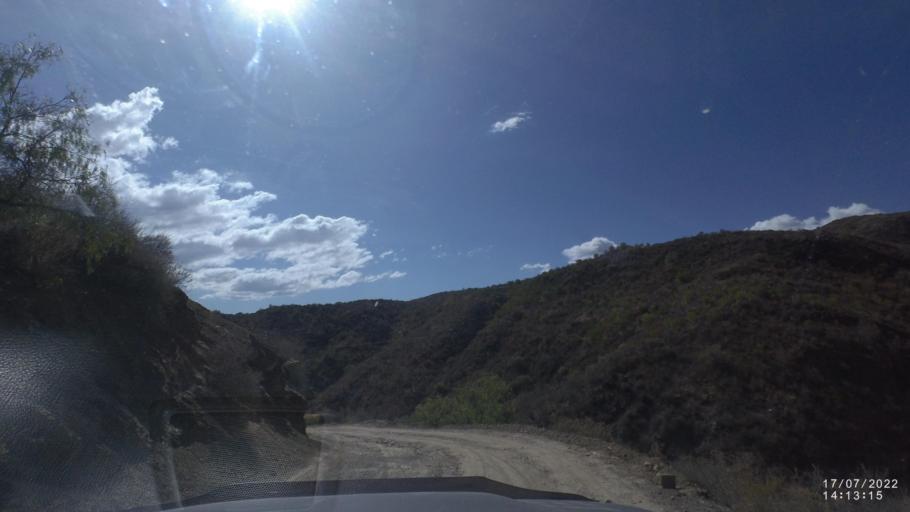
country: BO
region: Cochabamba
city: Capinota
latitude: -17.6869
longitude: -66.1854
